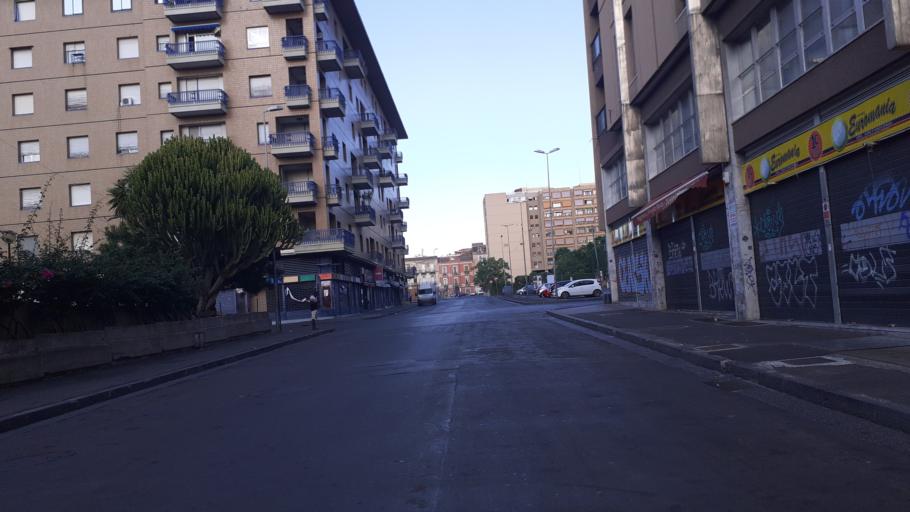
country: IT
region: Sicily
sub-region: Catania
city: Catania
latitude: 37.5083
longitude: 15.0895
